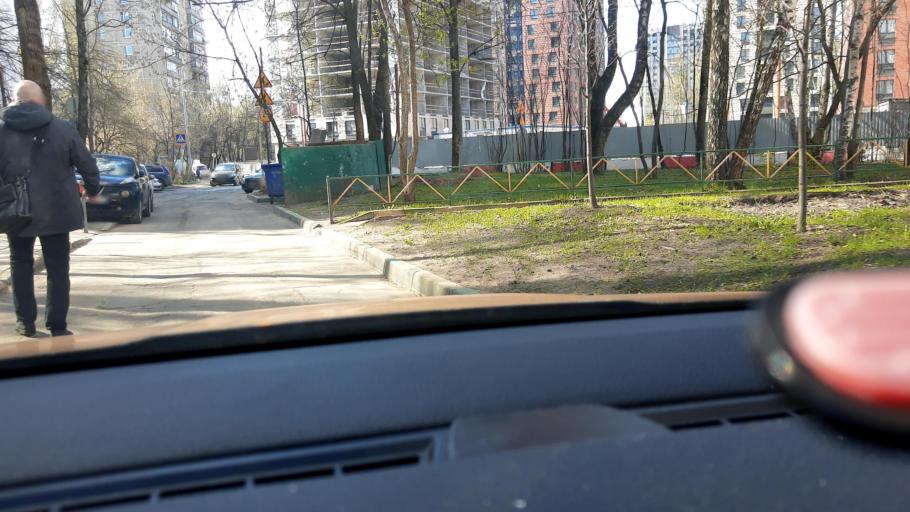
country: RU
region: Moskovskaya
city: Bol'shaya Setun'
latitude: 55.7450
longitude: 37.4087
